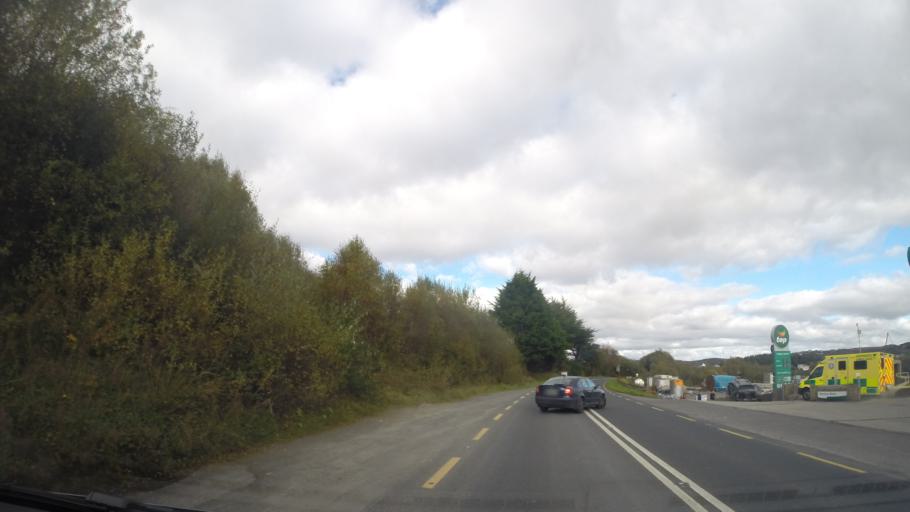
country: IE
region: Ulster
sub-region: County Donegal
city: Killybegs
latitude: 54.6470
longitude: -8.4310
